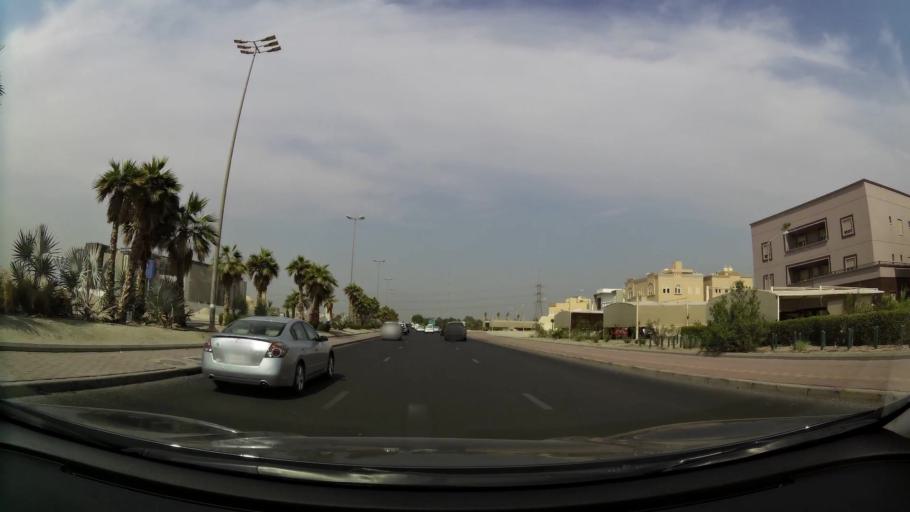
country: KW
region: Al Farwaniyah
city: Janub as Surrah
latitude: 29.3005
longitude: 48.0018
